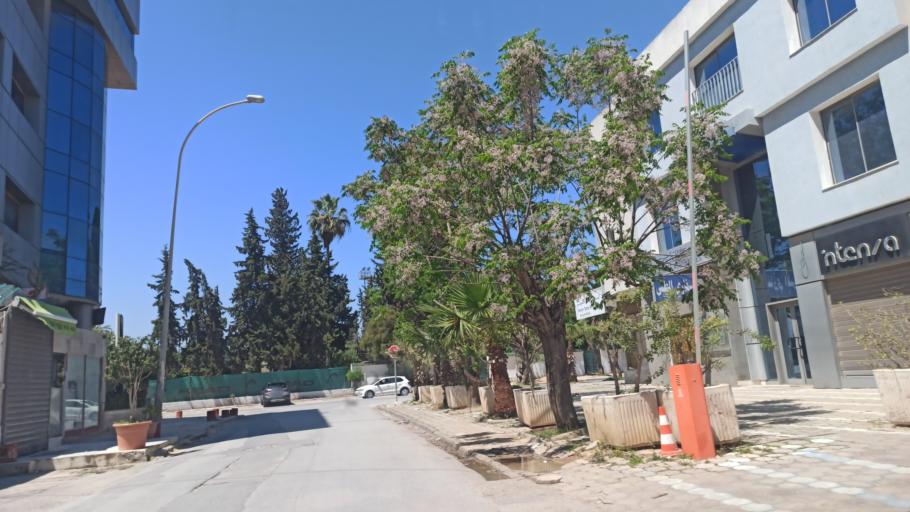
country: TN
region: Tunis
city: Tunis
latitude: 36.8251
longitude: 10.1827
